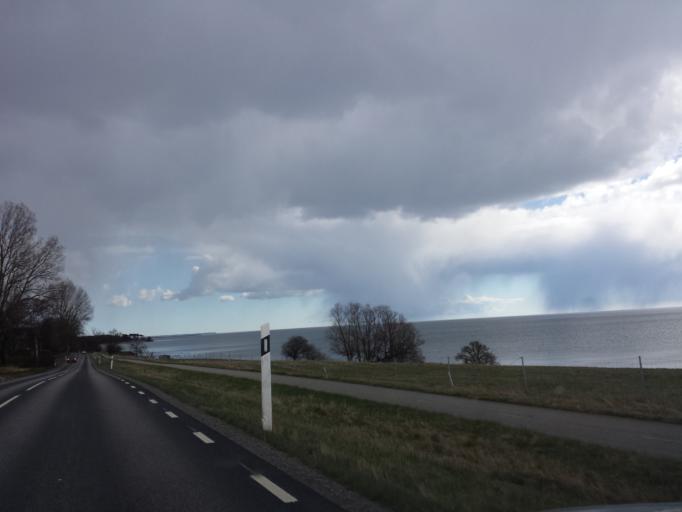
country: SE
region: Skane
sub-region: Ystads Kommun
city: Ystad
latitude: 55.4266
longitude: 13.7440
